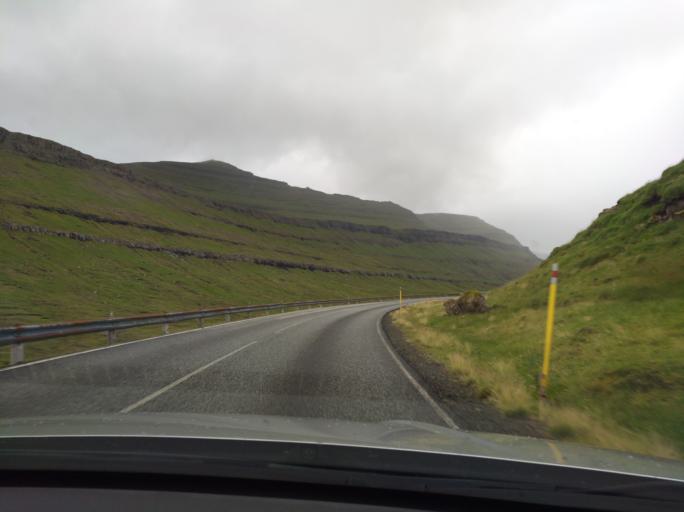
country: FO
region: Eysturoy
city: Fuglafjordur
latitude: 62.2237
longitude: -6.8796
